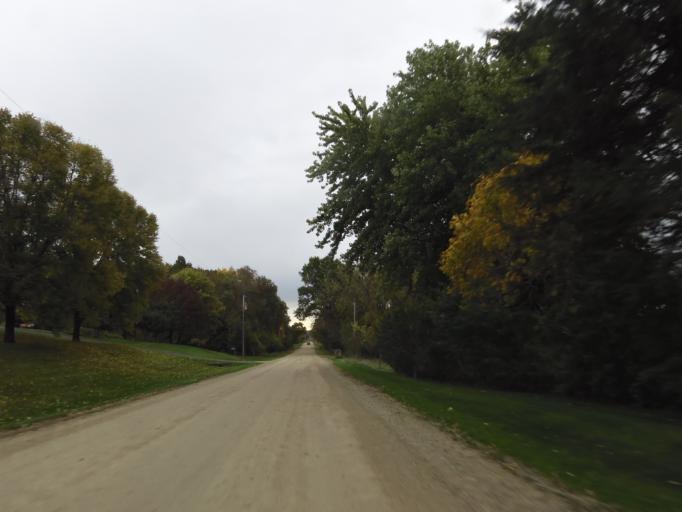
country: US
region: Minnesota
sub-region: Scott County
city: Prior Lake
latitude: 44.7036
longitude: -93.5081
